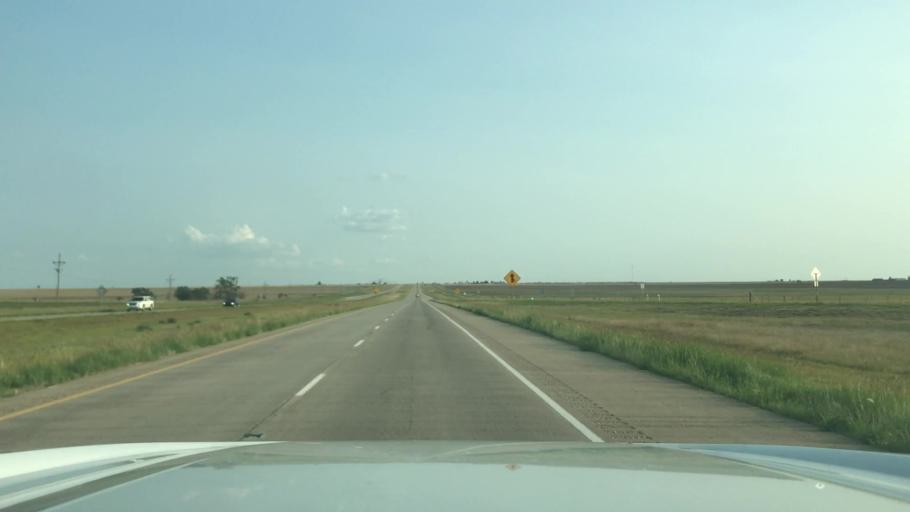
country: US
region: Texas
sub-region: Randall County
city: Canyon
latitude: 34.8361
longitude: -101.8489
